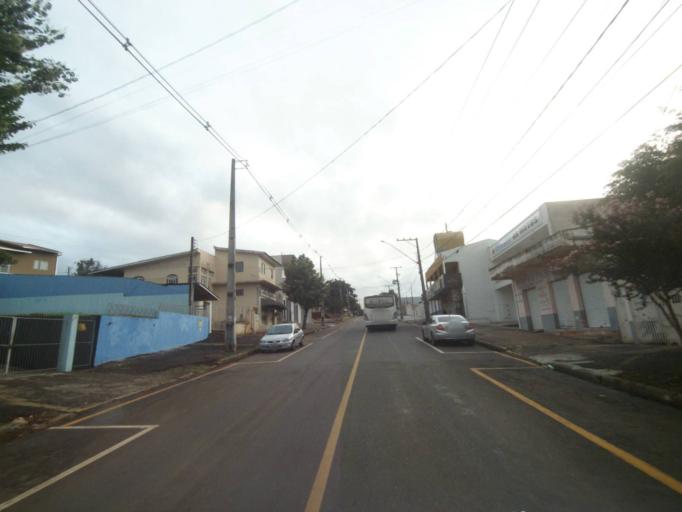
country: BR
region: Parana
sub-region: Telemaco Borba
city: Telemaco Borba
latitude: -24.3309
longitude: -50.6329
